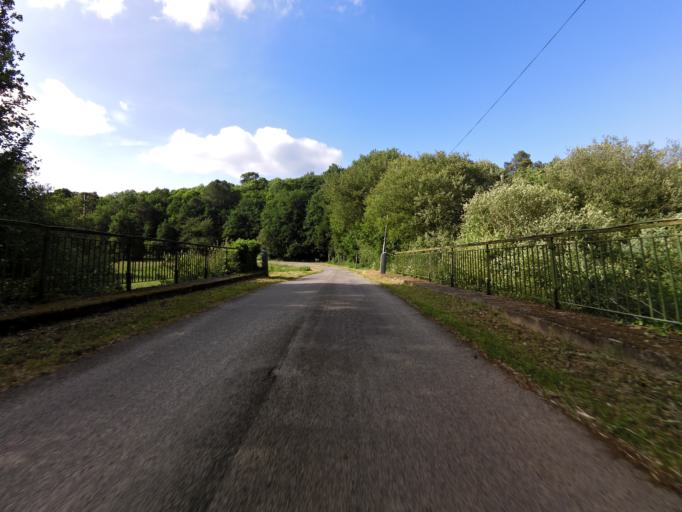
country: FR
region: Brittany
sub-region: Departement du Morbihan
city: Molac
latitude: 47.7184
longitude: -2.4140
